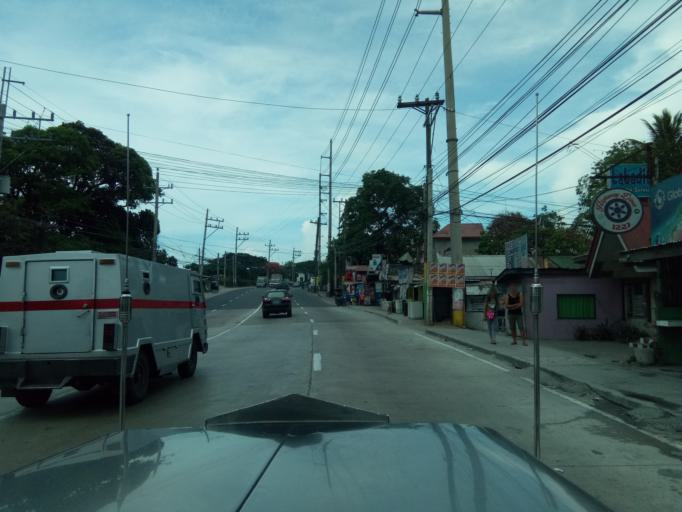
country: PH
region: Calabarzon
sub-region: Province of Cavite
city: Manggahan
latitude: 14.2929
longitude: 120.9356
